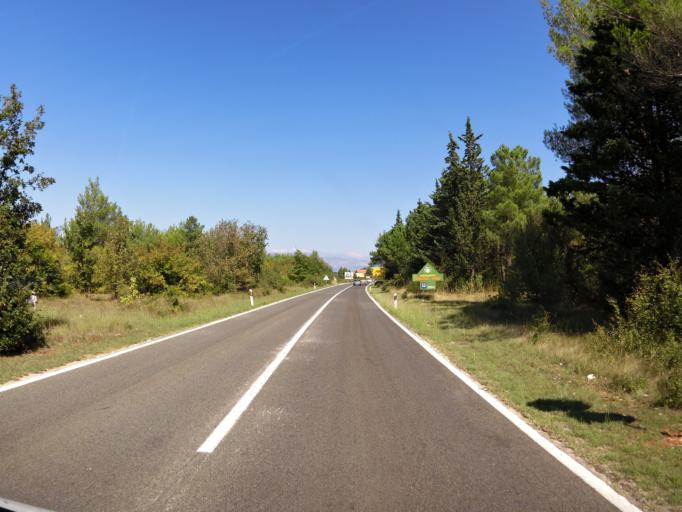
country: HR
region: Zadarska
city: Policnik
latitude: 44.1665
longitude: 15.3555
